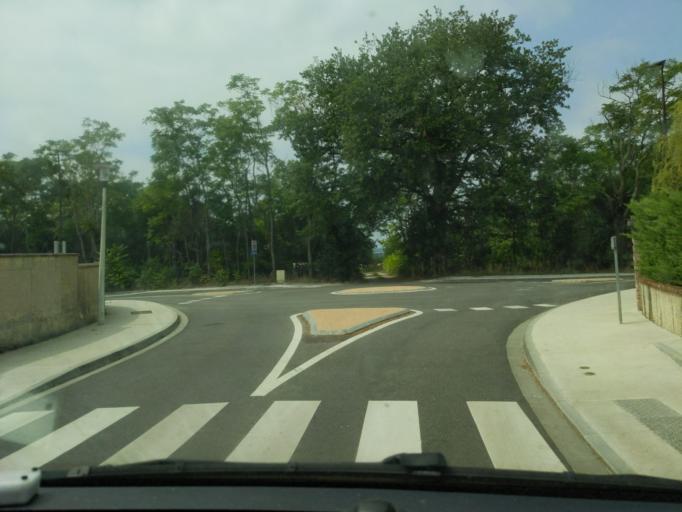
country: FR
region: Midi-Pyrenees
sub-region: Departement de la Haute-Garonne
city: Labege
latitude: 43.5325
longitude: 1.5412
